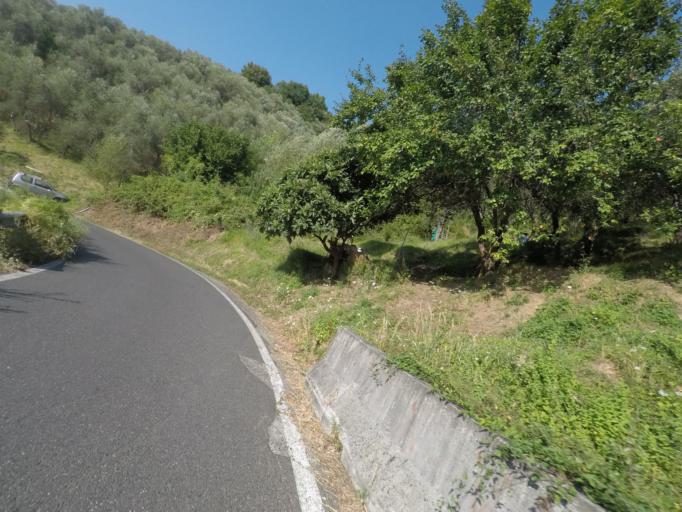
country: IT
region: Liguria
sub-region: Provincia di La Spezia
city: Casano-Dogana-Isola
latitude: 44.0900
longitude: 10.0497
